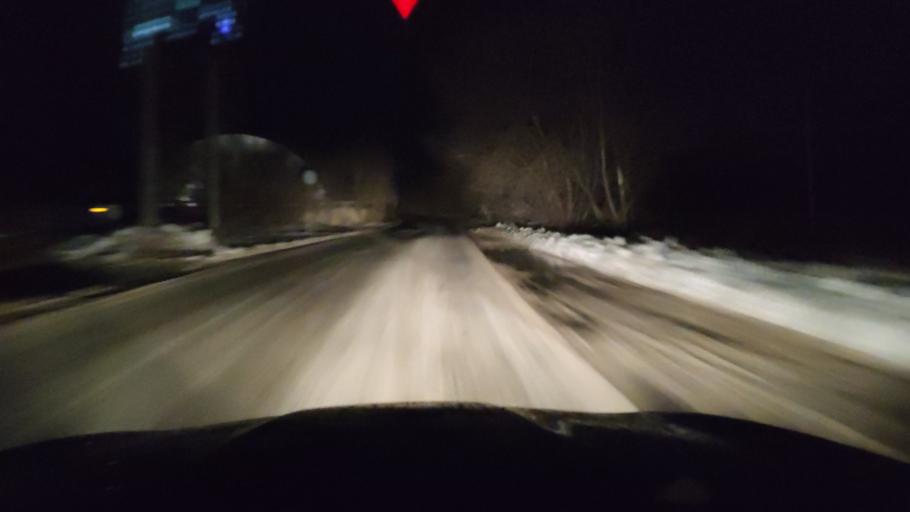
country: RU
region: Samara
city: Povolzhskiy
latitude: 53.5725
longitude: 49.6789
